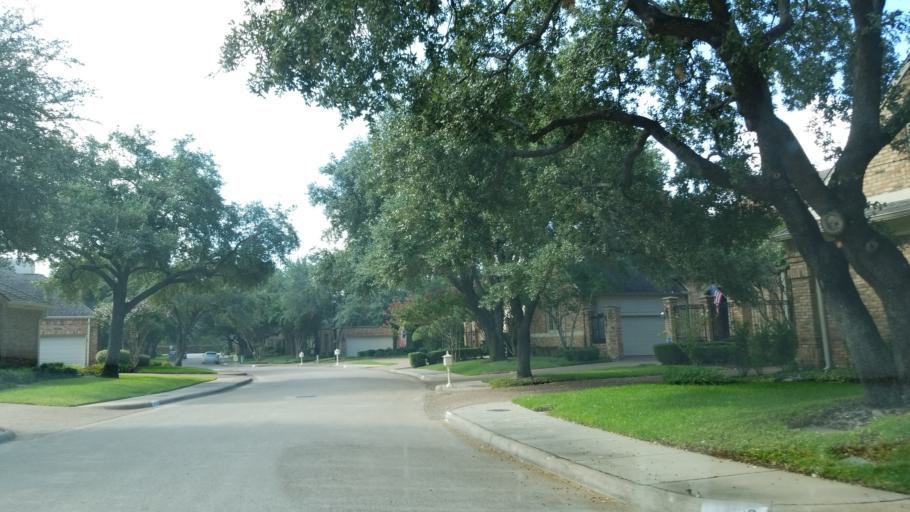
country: US
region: Texas
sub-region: Dallas County
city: Addison
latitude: 32.9349
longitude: -96.7893
